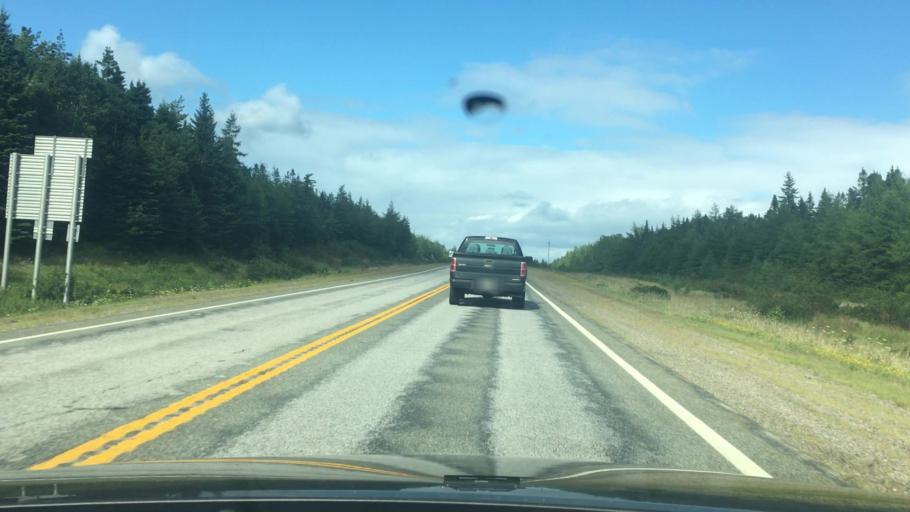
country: CA
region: Nova Scotia
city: Princeville
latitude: 45.6152
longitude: -61.0551
